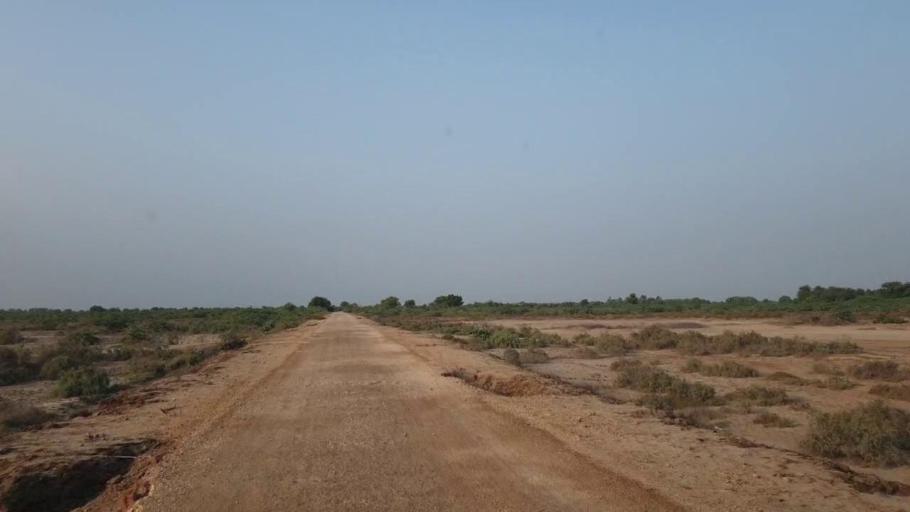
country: PK
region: Sindh
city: Rajo Khanani
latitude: 25.0243
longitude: 68.9773
